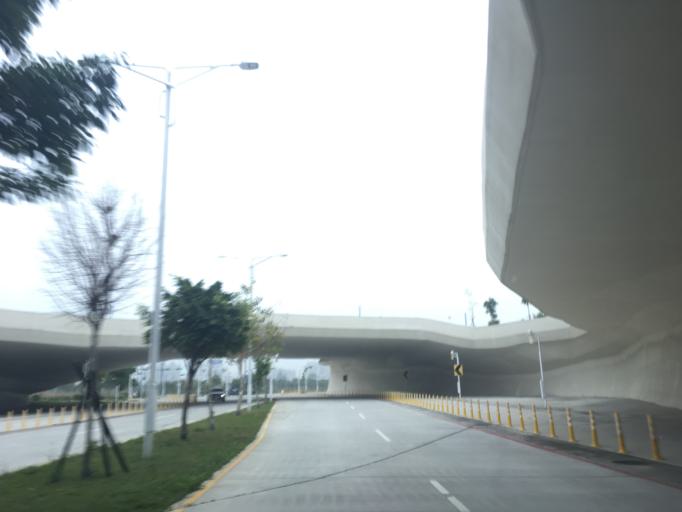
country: TW
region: Taiwan
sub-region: Taichung City
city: Taichung
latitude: 24.1848
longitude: 120.6540
